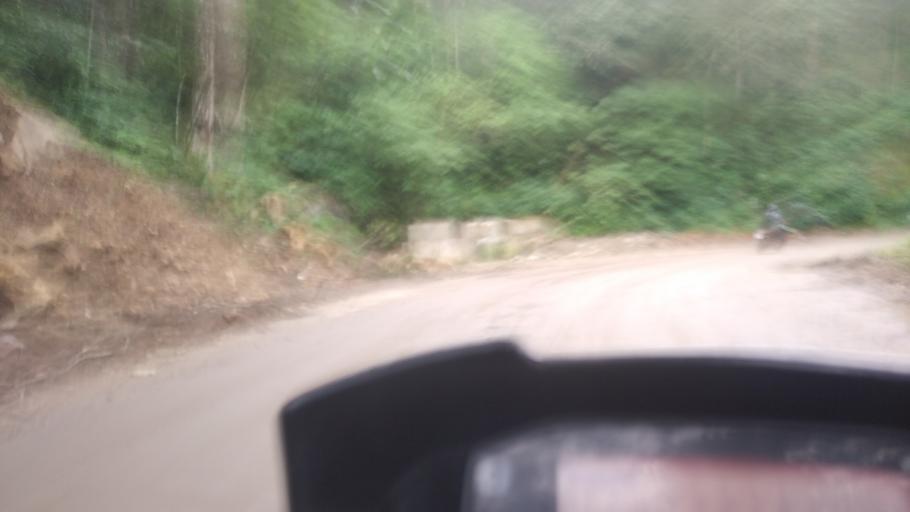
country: IN
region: Kerala
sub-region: Idukki
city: Munnar
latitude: 10.0359
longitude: 77.1404
